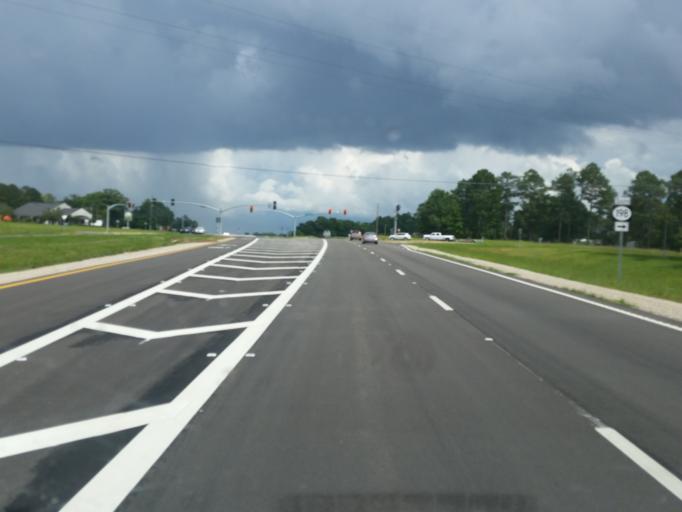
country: US
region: Mississippi
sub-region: George County
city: Lucedale
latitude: 30.9263
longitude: -88.5157
